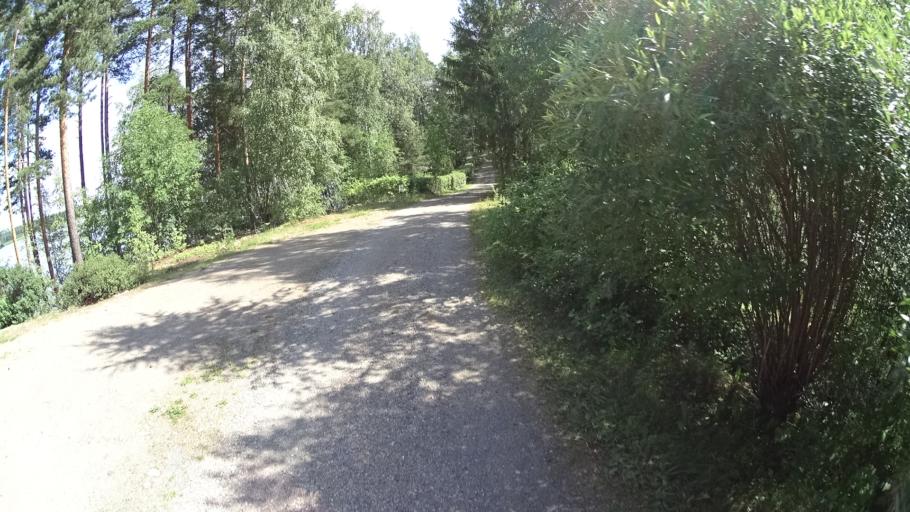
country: FI
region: Haeme
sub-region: Forssa
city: Tammela
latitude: 60.7674
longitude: 23.8842
